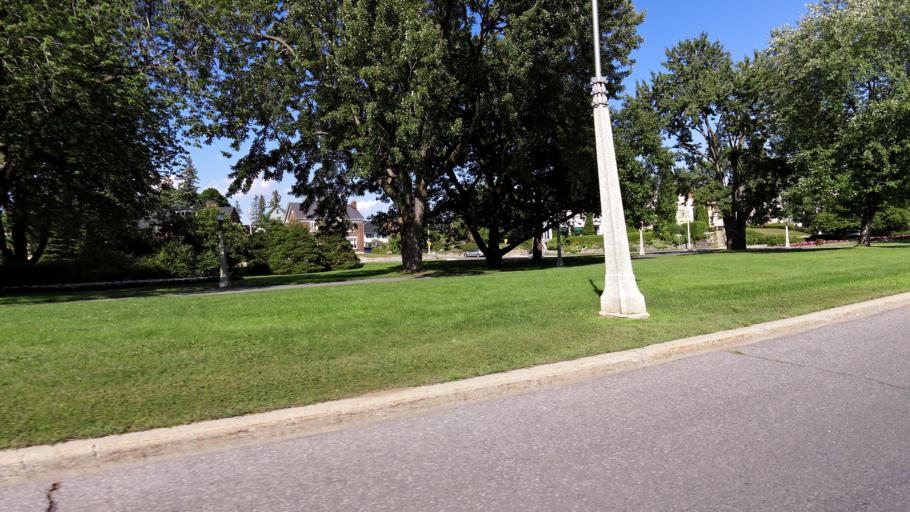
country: CA
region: Ontario
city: Ottawa
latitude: 45.3968
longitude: -75.7012
